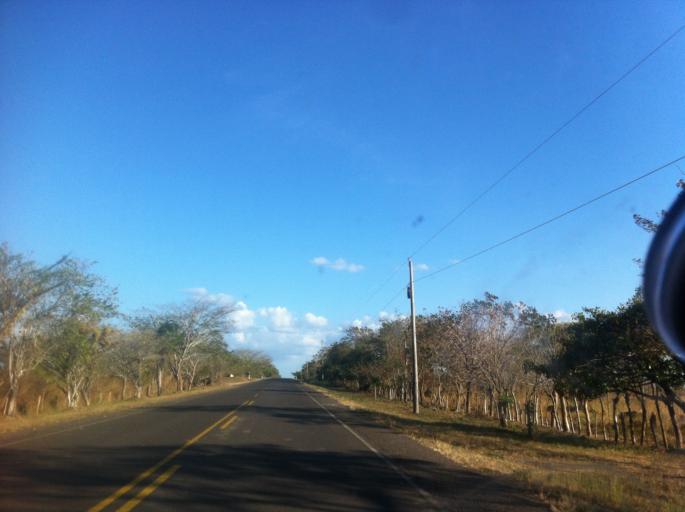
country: NI
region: Rio San Juan
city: Morrito
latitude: 11.7449
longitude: -84.9899
